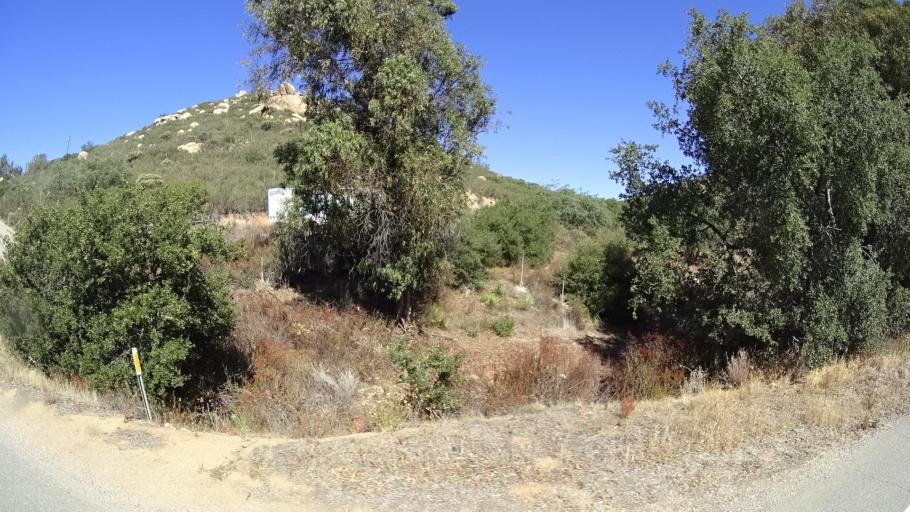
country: US
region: California
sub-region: San Diego County
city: Descanso
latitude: 32.8012
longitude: -116.6464
